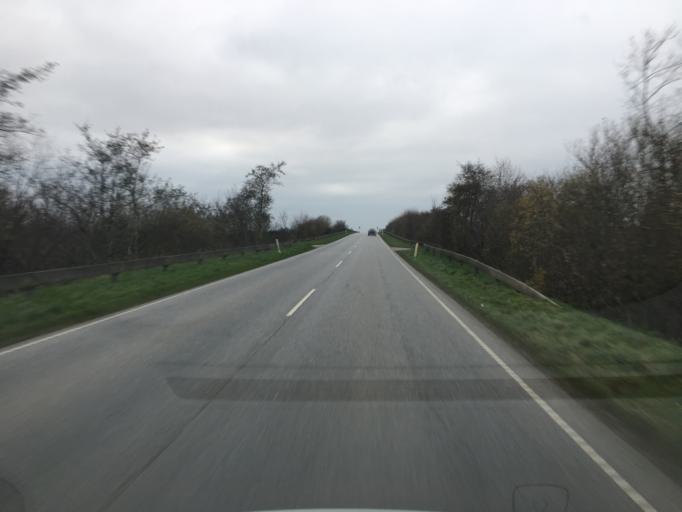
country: DK
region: South Denmark
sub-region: Aabenraa Kommune
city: Rodekro
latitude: 55.0203
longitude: 9.3108
